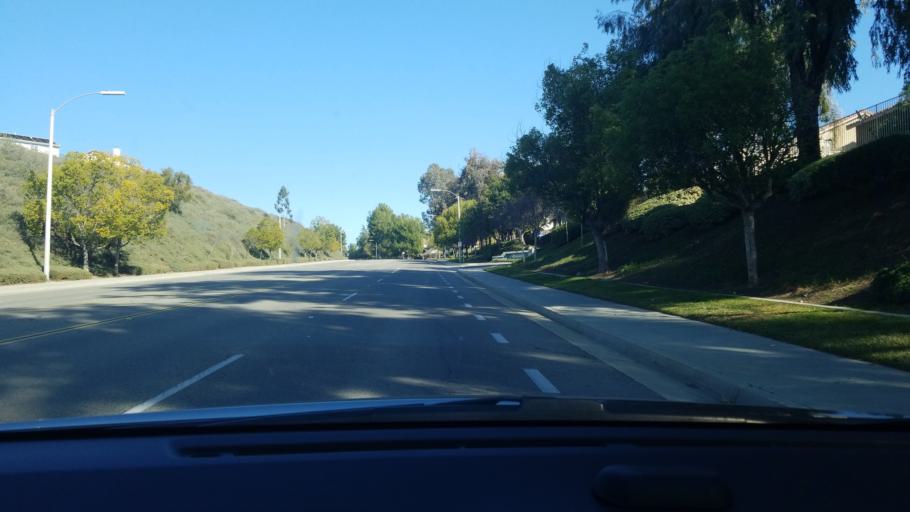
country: US
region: California
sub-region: Riverside County
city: Murrieta
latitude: 33.5914
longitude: -117.2091
